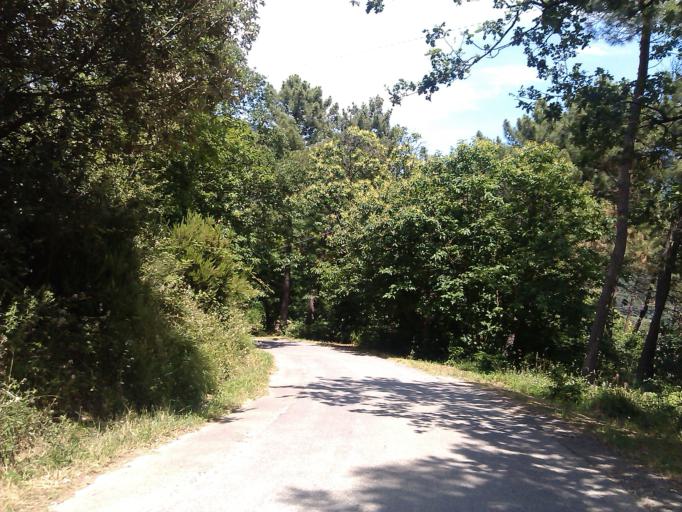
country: IT
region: Tuscany
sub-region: Provincia di Pistoia
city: Montale
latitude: 43.9677
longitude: 11.0402
